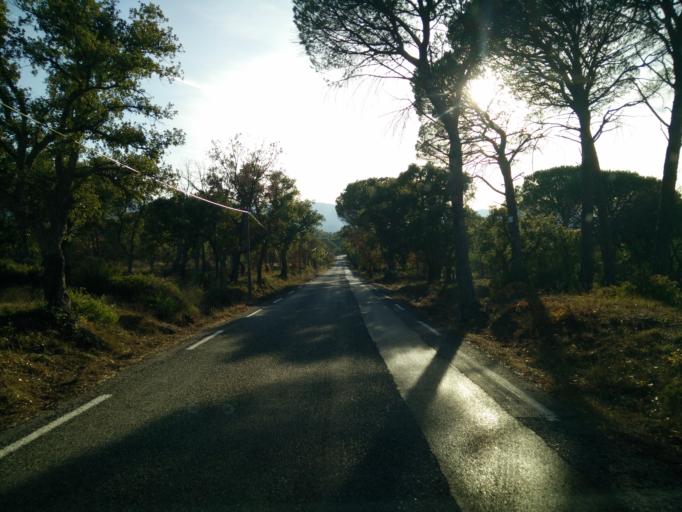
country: FR
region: Provence-Alpes-Cote d'Azur
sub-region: Departement du Var
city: La Garde-Freinet
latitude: 43.3633
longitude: 6.4456
